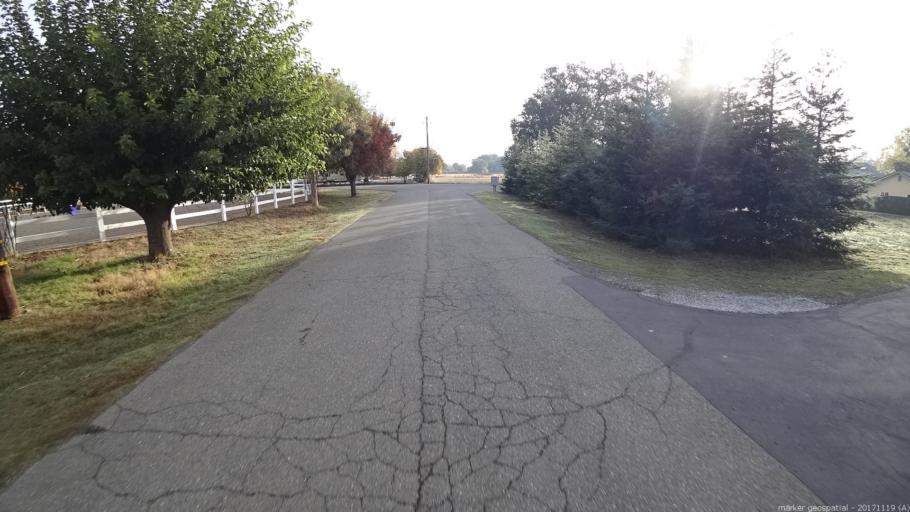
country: US
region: California
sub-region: Shasta County
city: Anderson
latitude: 40.5043
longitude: -122.3441
